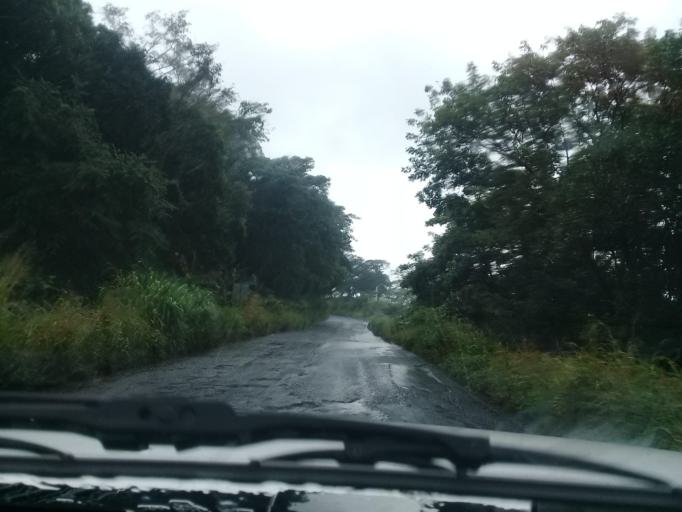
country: MX
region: Veracruz
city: Santiago Tuxtla
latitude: 18.4612
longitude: -95.2961
